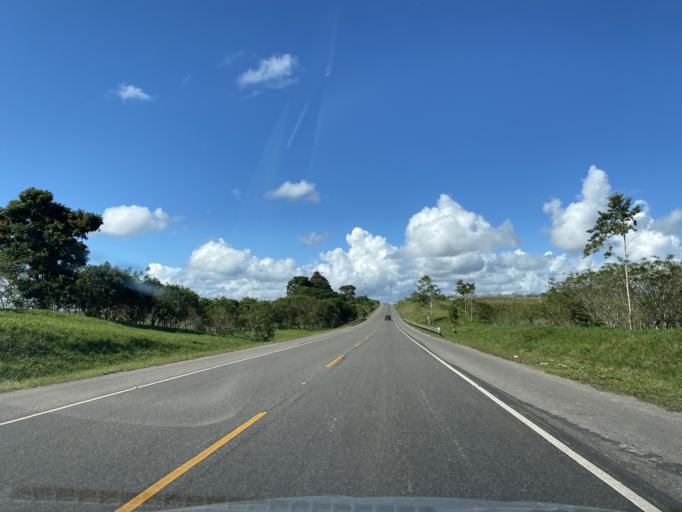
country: DO
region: Monte Plata
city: Majagual
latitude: 18.9981
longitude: -69.8176
